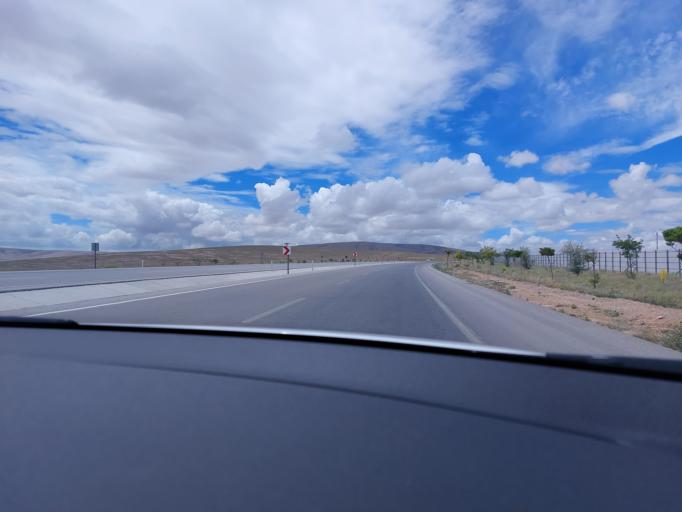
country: TR
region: Konya
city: Obruk
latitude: 38.0644
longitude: 33.0603
